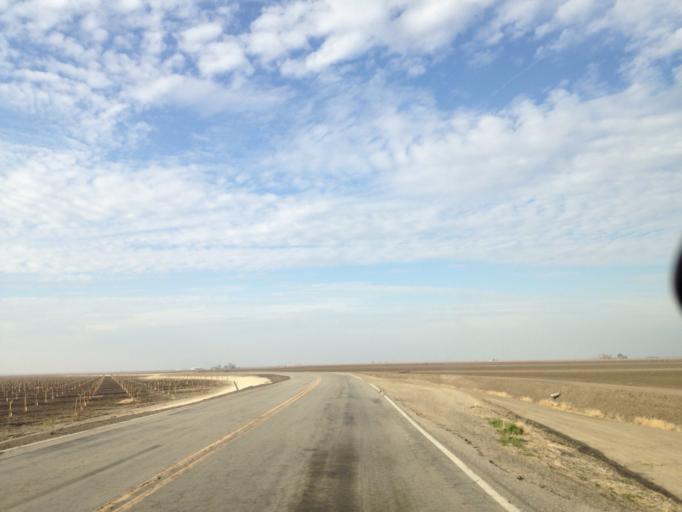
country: US
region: California
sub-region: Kern County
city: Buttonwillow
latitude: 35.4418
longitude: -119.5503
